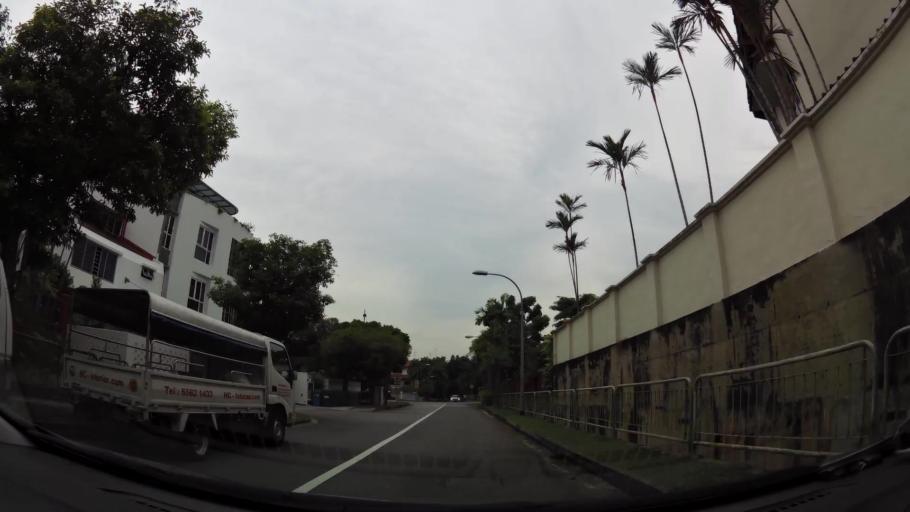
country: SG
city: Singapore
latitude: 1.3565
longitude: 103.8685
